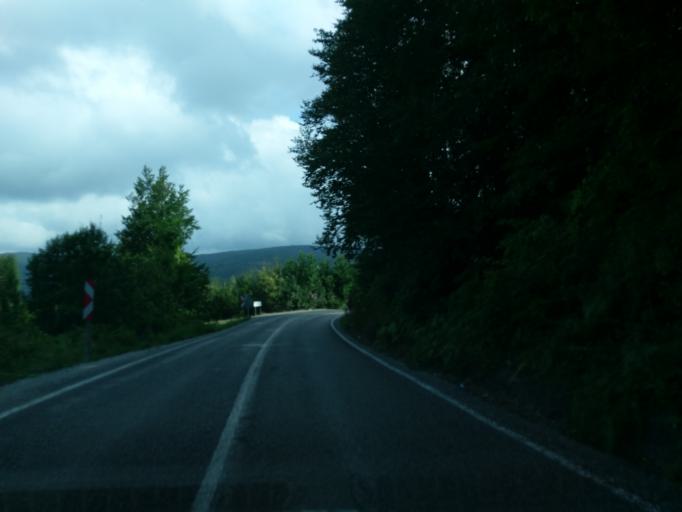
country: TR
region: Sinop
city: Ayancik
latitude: 41.8821
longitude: 34.5142
